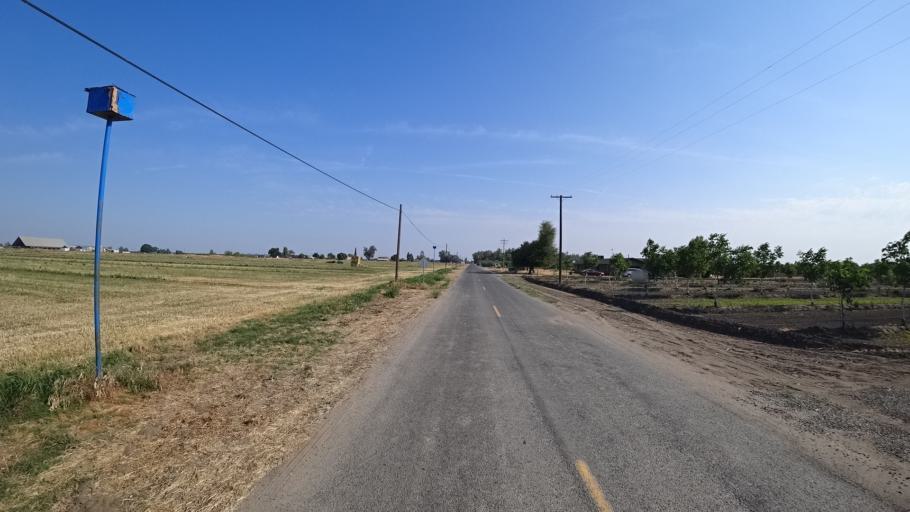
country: US
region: California
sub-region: Fresno County
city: Riverdale
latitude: 36.3752
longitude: -119.8162
